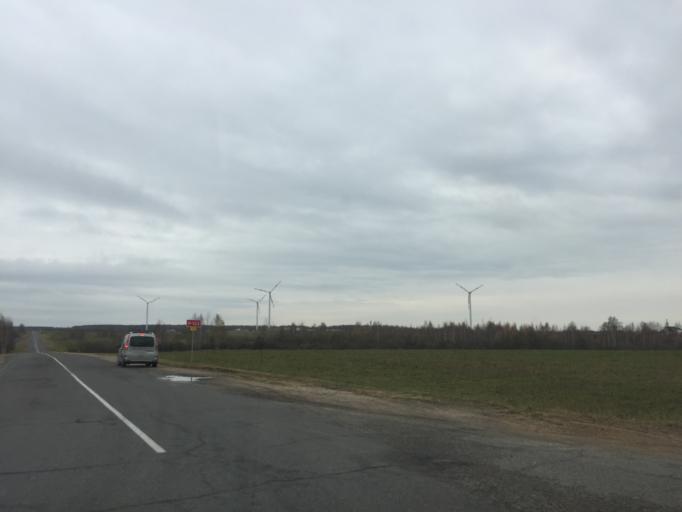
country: BY
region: Mogilev
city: Drybin
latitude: 54.1382
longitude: 31.1098
